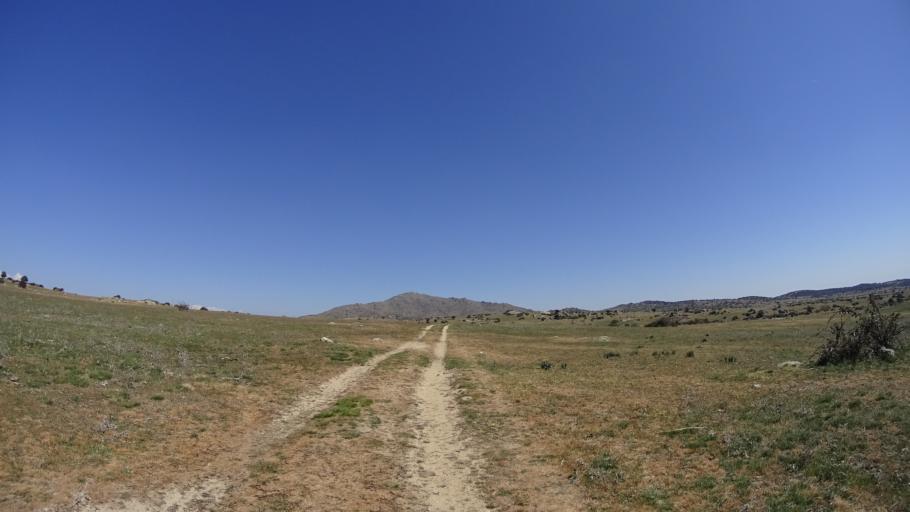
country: ES
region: Madrid
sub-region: Provincia de Madrid
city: Colmenar Viejo
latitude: 40.7030
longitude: -3.7588
